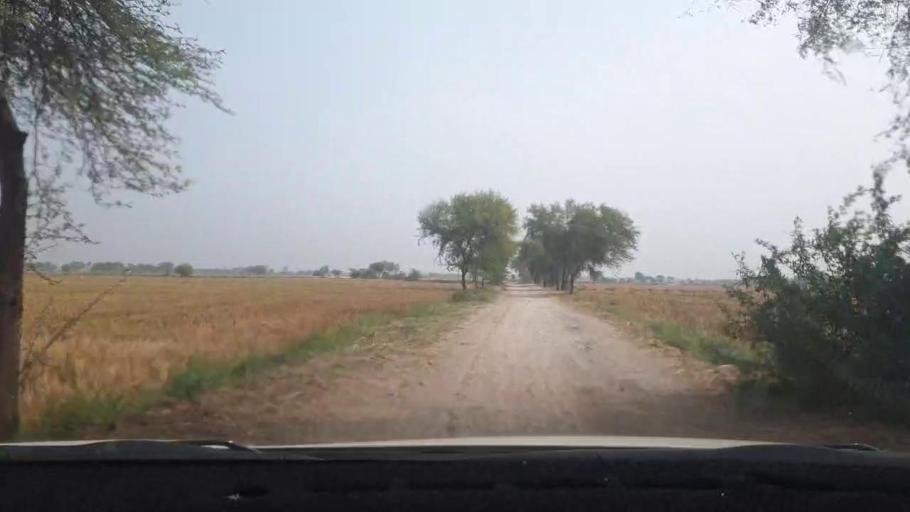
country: PK
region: Sindh
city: Tando Muhammad Khan
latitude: 25.0599
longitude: 68.5409
